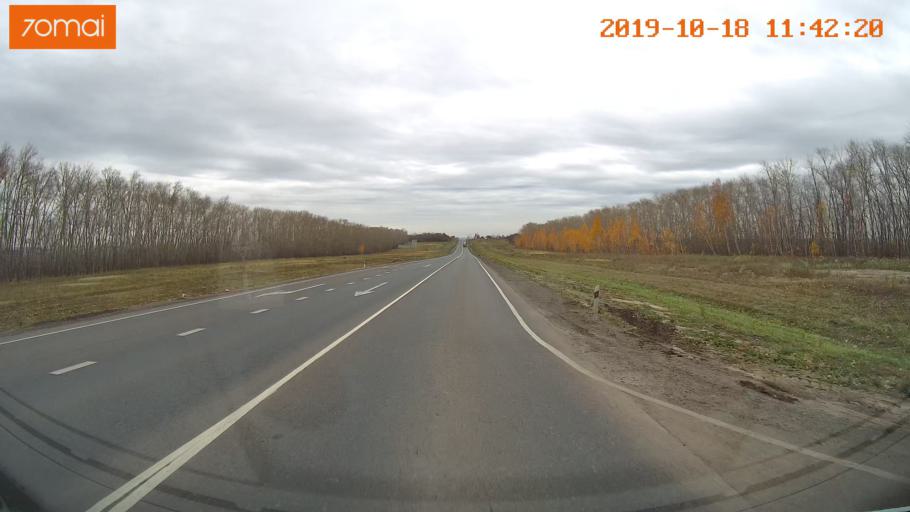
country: RU
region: Rjazan
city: Oktyabr'skiy
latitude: 54.1872
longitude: 38.9257
